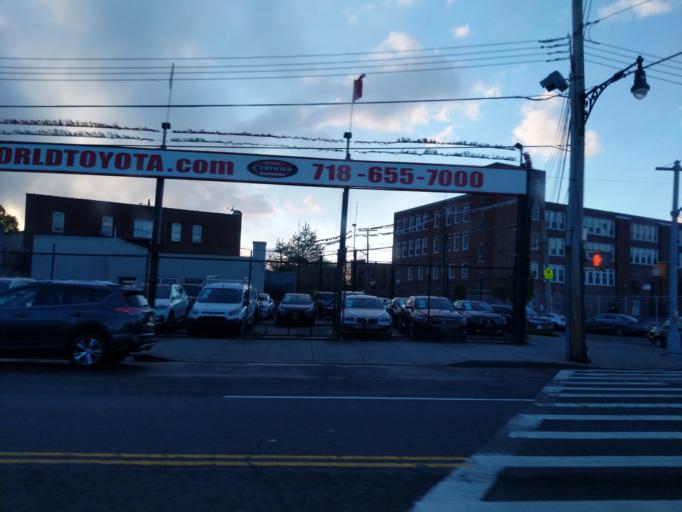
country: US
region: New York
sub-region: Bronx
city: Eastchester
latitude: 40.8744
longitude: -73.8522
